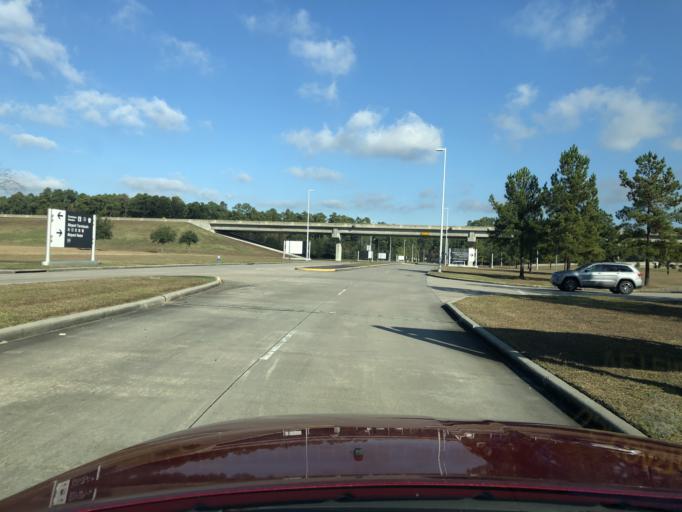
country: US
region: Texas
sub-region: Harris County
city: Aldine
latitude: 29.9682
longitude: -95.3354
